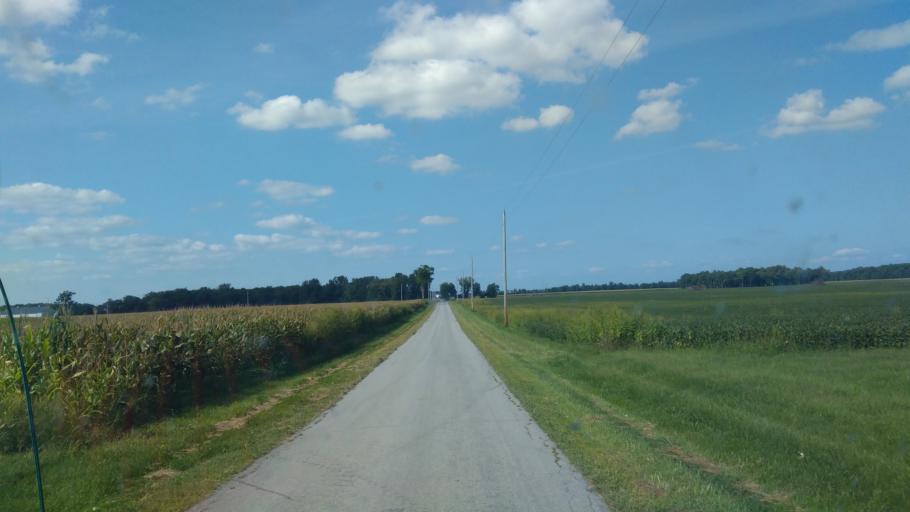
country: US
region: Ohio
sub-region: Hardin County
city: Forest
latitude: 40.7202
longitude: -83.4779
